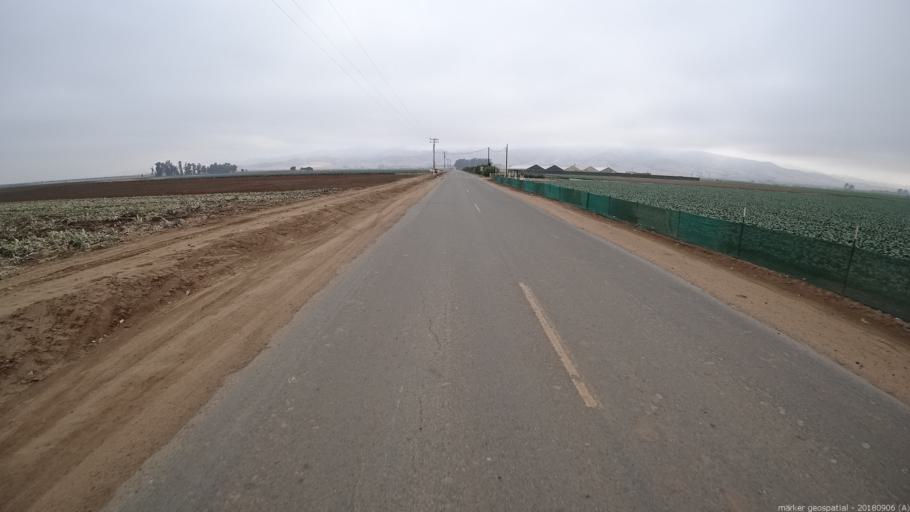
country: US
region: California
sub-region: Monterey County
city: Chualar
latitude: 36.6436
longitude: -121.5683
